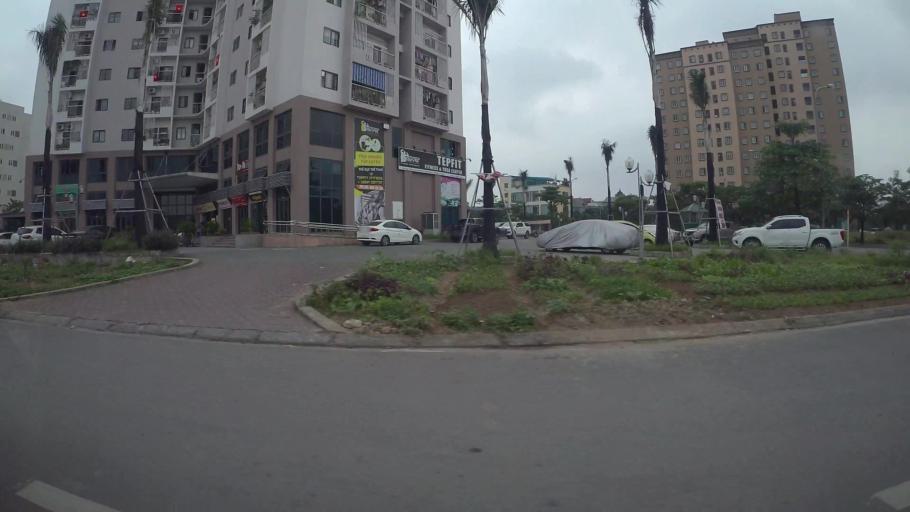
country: VN
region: Ha Noi
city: Trau Quy
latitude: 21.0596
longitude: 105.9136
